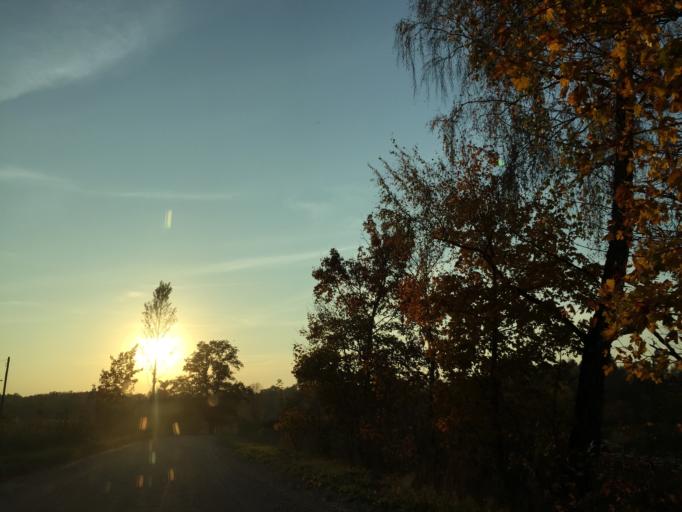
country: LV
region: Priekule
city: Priekule
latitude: 56.4802
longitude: 21.7262
